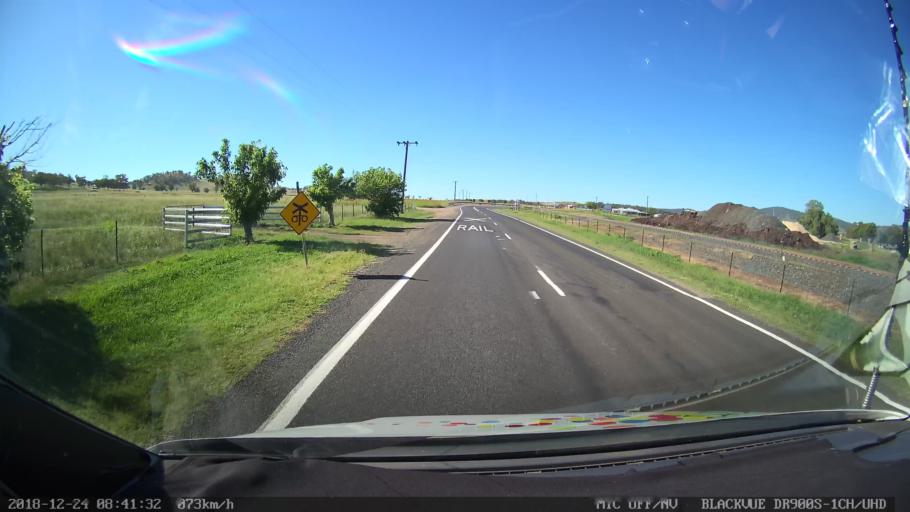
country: AU
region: New South Wales
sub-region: Liverpool Plains
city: Quirindi
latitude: -31.3642
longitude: 150.6450
